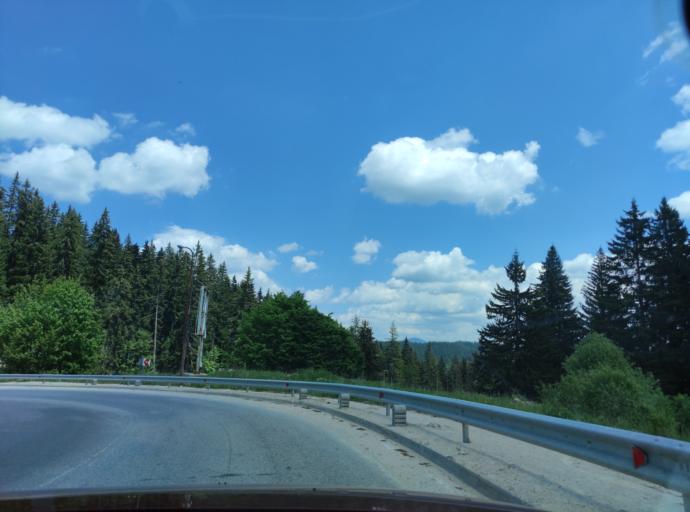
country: BG
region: Smolyan
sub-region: Obshtina Smolyan
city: Smolyan
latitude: 41.6505
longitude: 24.6986
